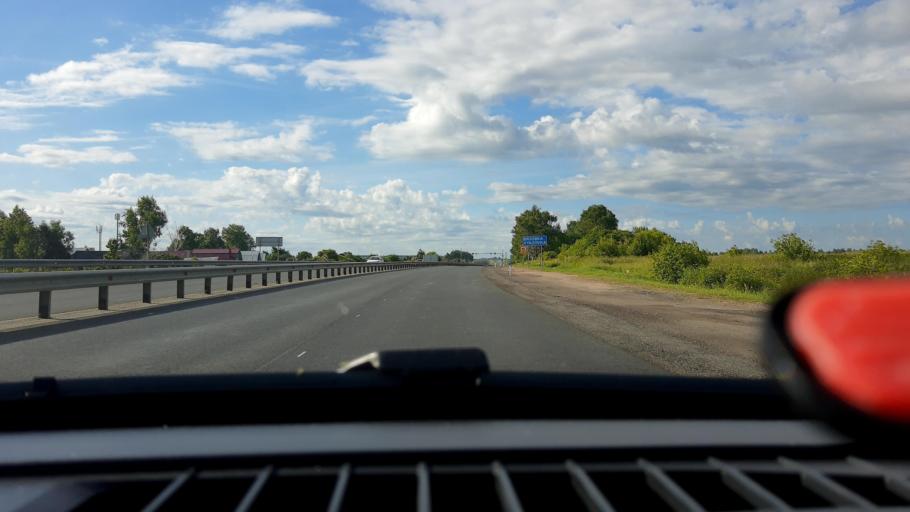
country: RU
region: Nizjnij Novgorod
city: Burevestnik
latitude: 56.1429
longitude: 43.9121
